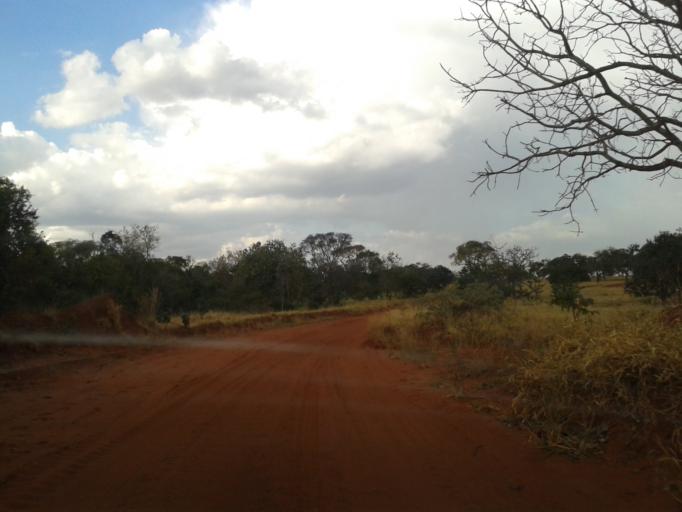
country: BR
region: Minas Gerais
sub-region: Santa Vitoria
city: Santa Vitoria
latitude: -19.1920
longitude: -49.8761
